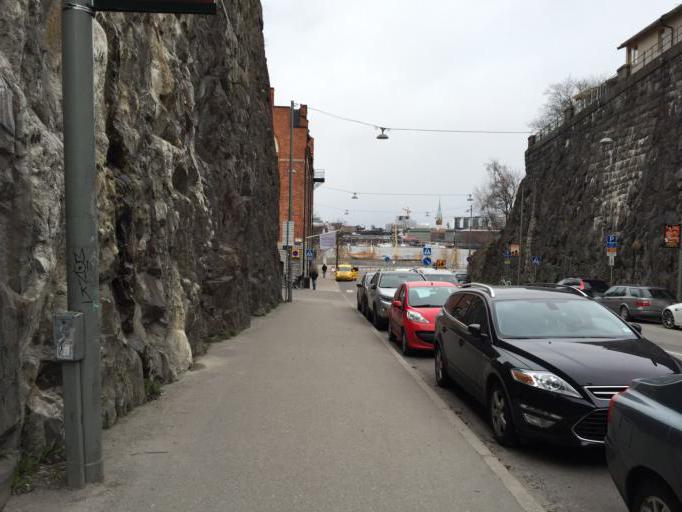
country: SE
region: Stockholm
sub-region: Stockholms Kommun
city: Stockholm
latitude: 59.3197
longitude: 18.0565
